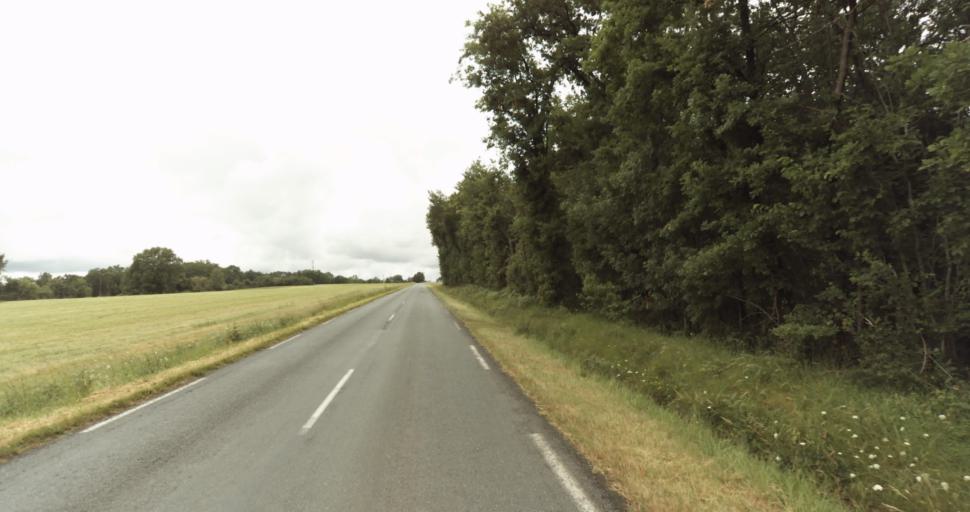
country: FR
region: Aquitaine
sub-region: Departement de la Dordogne
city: Beaumont-du-Perigord
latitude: 44.7438
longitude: 0.7807
